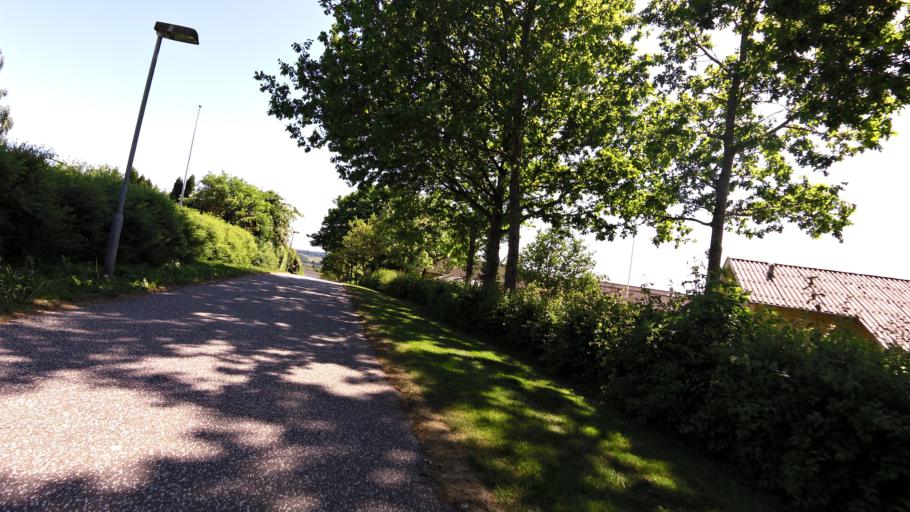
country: DK
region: Central Jutland
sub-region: Arhus Kommune
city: Framlev
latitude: 56.1438
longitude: 9.9930
